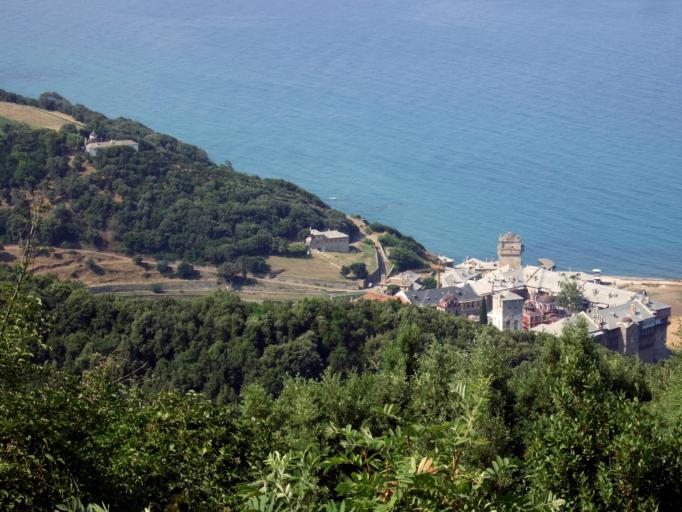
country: GR
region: Mount Athos
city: Karyes
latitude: 40.2374
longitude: 24.2822
